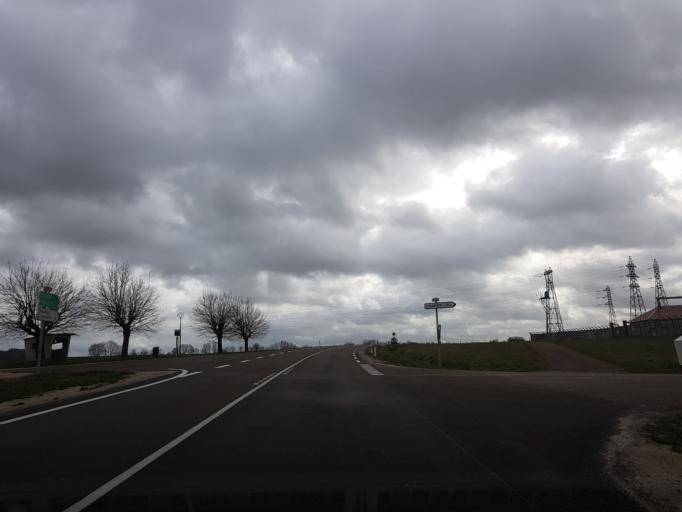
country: FR
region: Champagne-Ardenne
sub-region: Departement de la Haute-Marne
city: Rolampont
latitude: 47.9246
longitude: 5.2911
